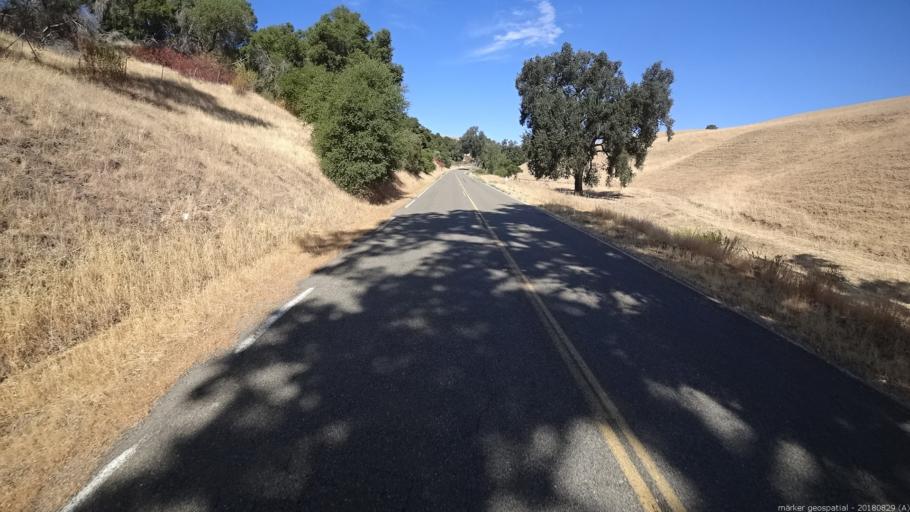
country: US
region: California
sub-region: San Luis Obispo County
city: Lake Nacimiento
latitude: 35.8399
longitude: -121.0420
